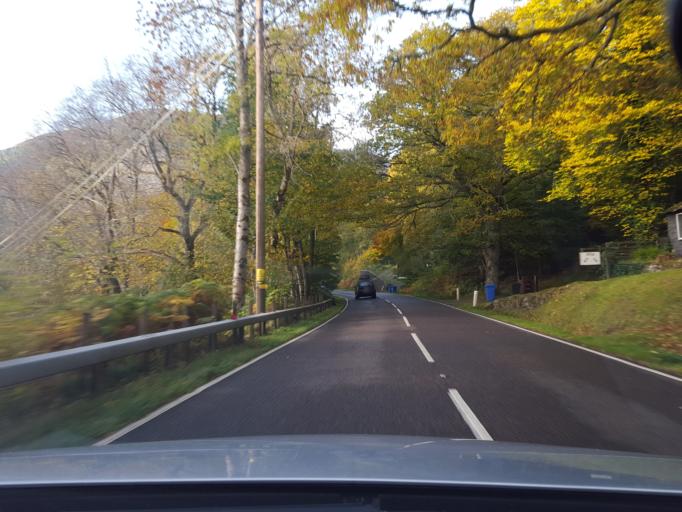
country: GB
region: Scotland
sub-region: Highland
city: Beauly
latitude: 57.2133
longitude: -4.5982
